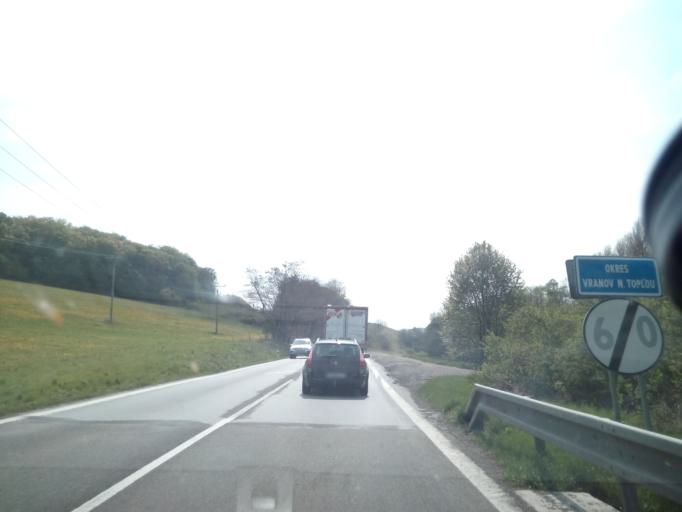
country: SK
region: Presovsky
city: Giraltovce
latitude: 49.0490
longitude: 21.4355
